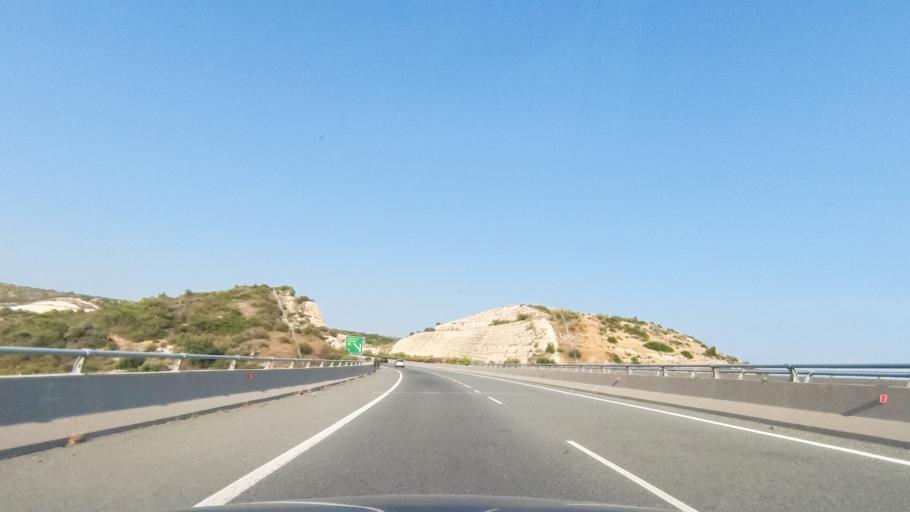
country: CY
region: Limassol
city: Sotira
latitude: 34.6784
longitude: 32.7963
